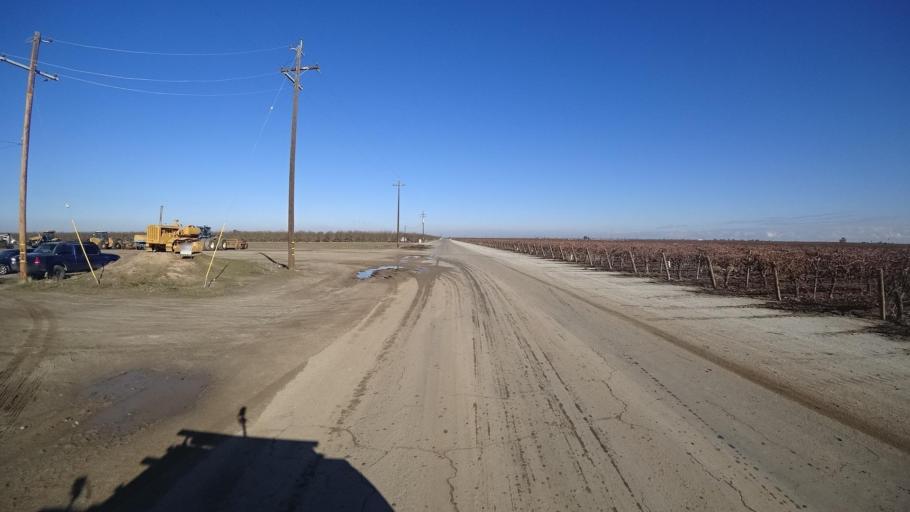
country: US
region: California
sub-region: Kern County
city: Delano
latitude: 35.7255
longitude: -119.2763
